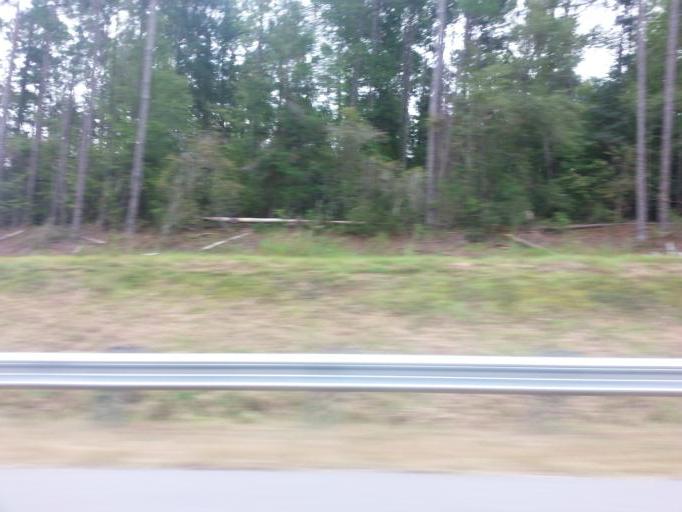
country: US
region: Alabama
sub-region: Conecuh County
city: Evergreen
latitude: 31.5441
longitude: -86.8833
